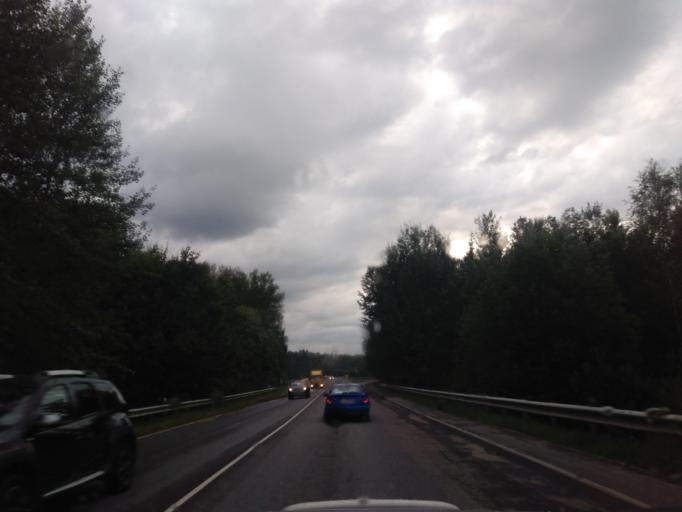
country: BY
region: Minsk
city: Enyerhyetykaw
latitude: 53.5894
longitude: 27.0454
